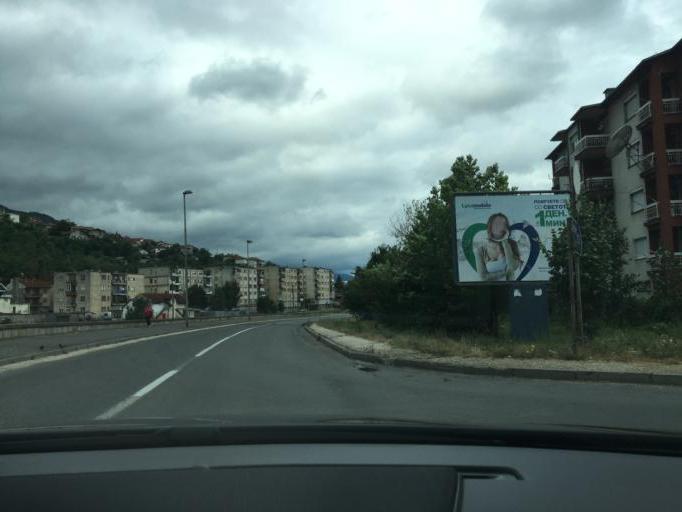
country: MK
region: Kriva Palanka
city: Kriva Palanka
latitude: 42.2014
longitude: 22.3329
